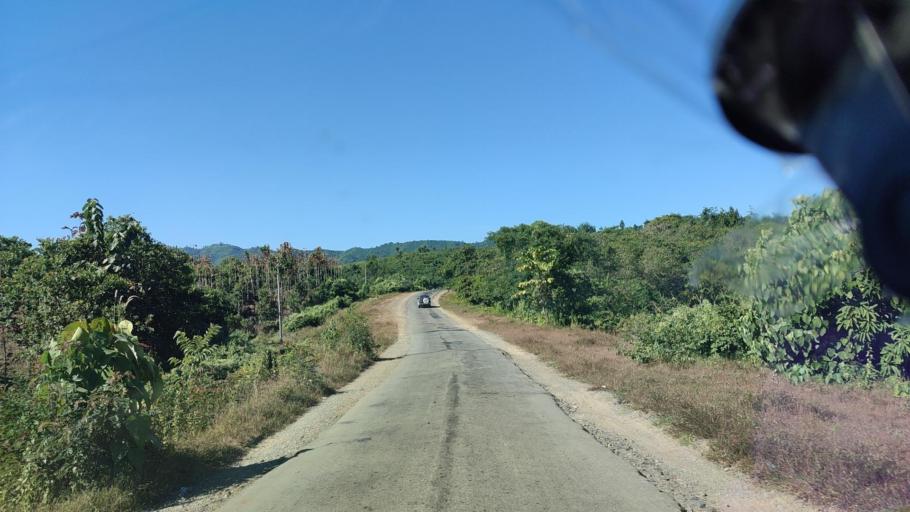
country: MM
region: Rakhine
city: Sittwe
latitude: 19.9857
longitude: 93.7068
